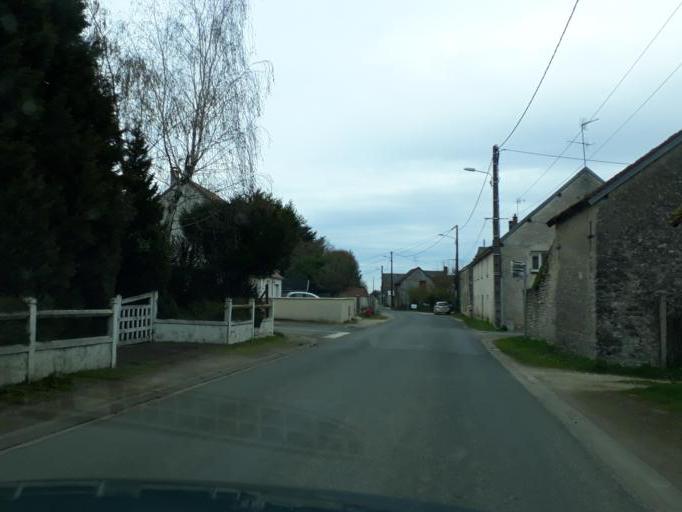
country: FR
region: Centre
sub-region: Departement du Loir-et-Cher
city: Villebarou
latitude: 47.6406
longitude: 1.2954
